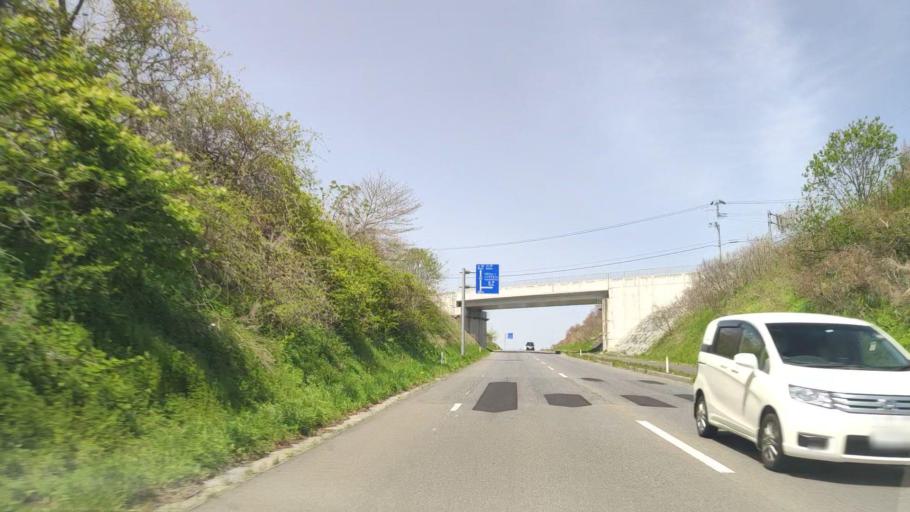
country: JP
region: Aomori
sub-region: Hachinohe Shi
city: Uchimaru
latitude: 40.5260
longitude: 141.4113
